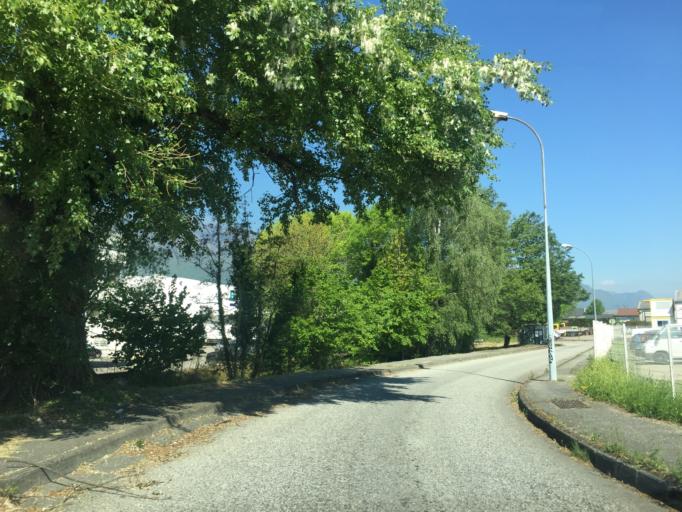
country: FR
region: Rhone-Alpes
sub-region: Departement de la Savoie
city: La Motte-Servolex
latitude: 45.5942
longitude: 5.8890
